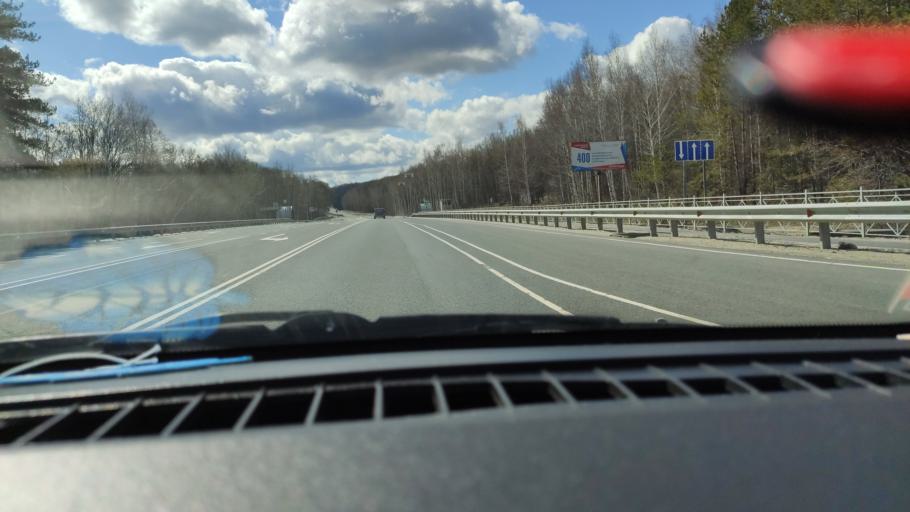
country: RU
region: Saratov
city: Khvalynsk
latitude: 52.5103
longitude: 48.0159
